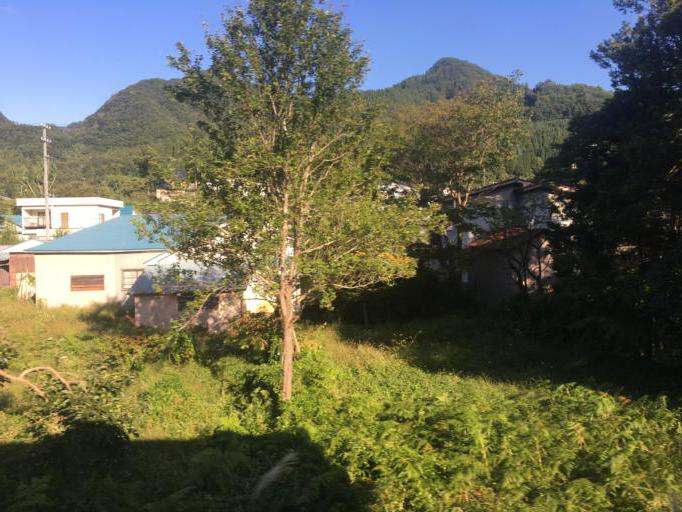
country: JP
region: Akita
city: Takanosu
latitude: 39.9954
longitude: 140.4011
